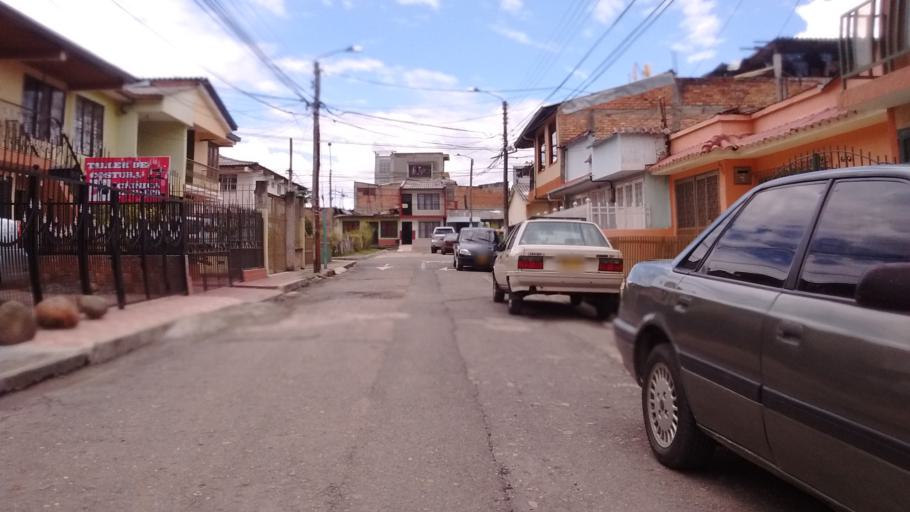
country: CO
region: Cauca
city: Popayan
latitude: 2.4569
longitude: -76.5881
